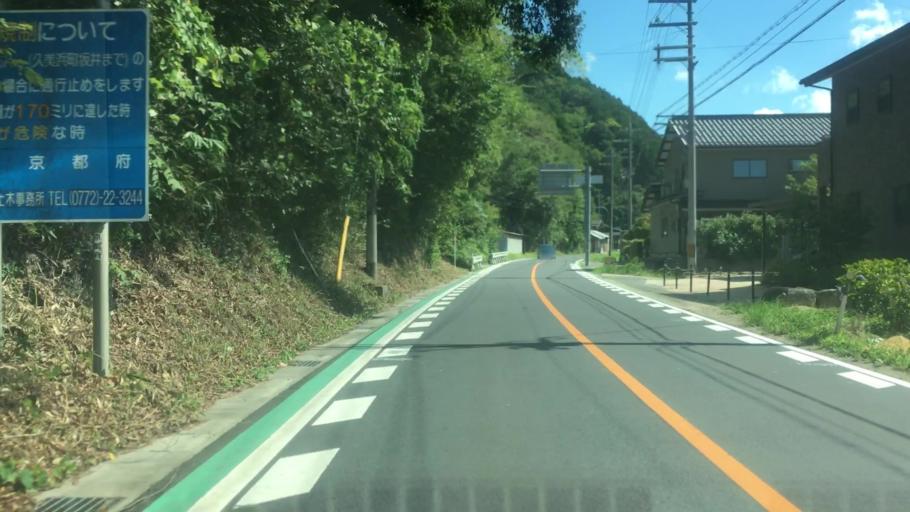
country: JP
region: Hyogo
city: Toyooka
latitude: 35.5982
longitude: 134.9045
